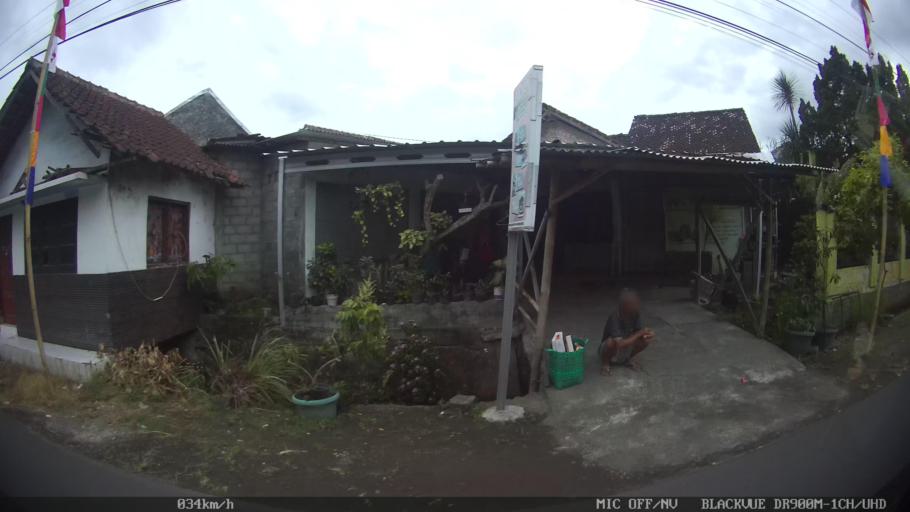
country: ID
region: Daerah Istimewa Yogyakarta
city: Sewon
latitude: -7.8370
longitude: 110.4149
